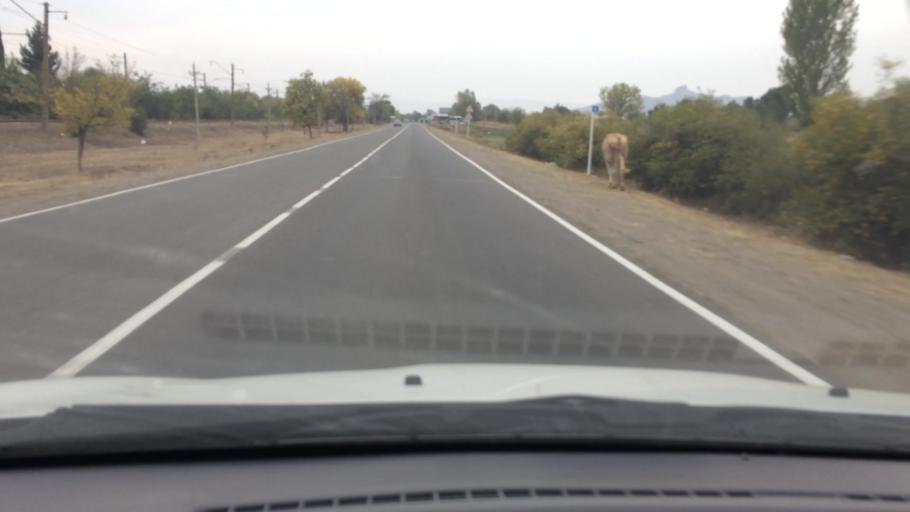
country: GE
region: Kvemo Kartli
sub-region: Marneuli
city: Marneuli
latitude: 41.4252
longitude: 44.8233
